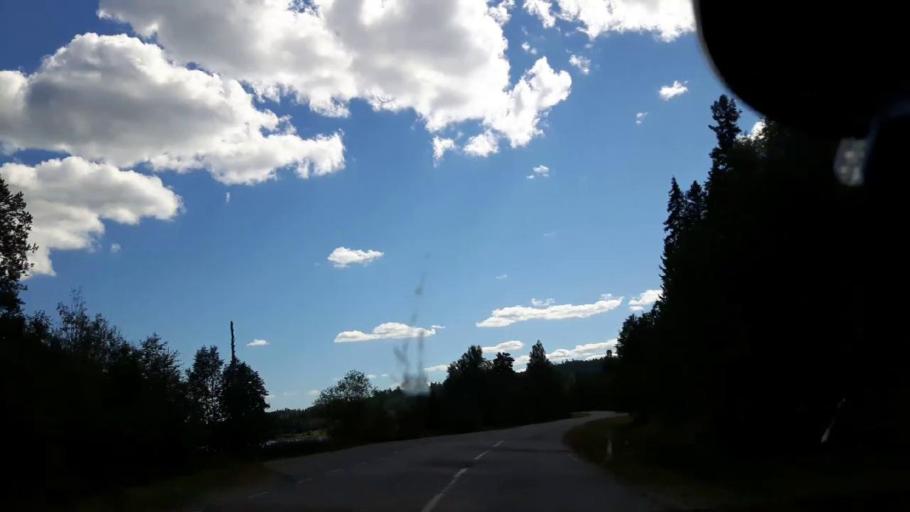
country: SE
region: Jaemtland
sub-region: Ragunda Kommun
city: Hammarstrand
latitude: 62.8398
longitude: 16.1746
